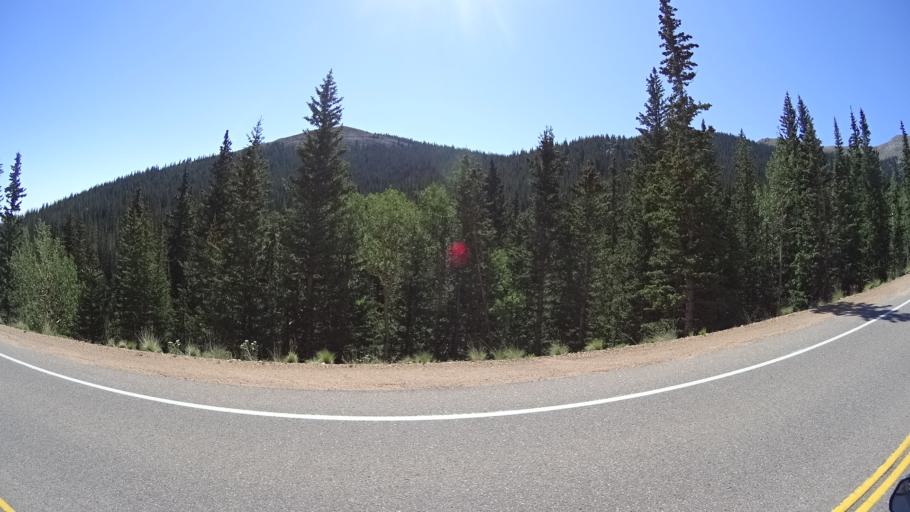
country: US
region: Colorado
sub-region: El Paso County
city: Cascade-Chipita Park
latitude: 38.8842
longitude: -105.0713
